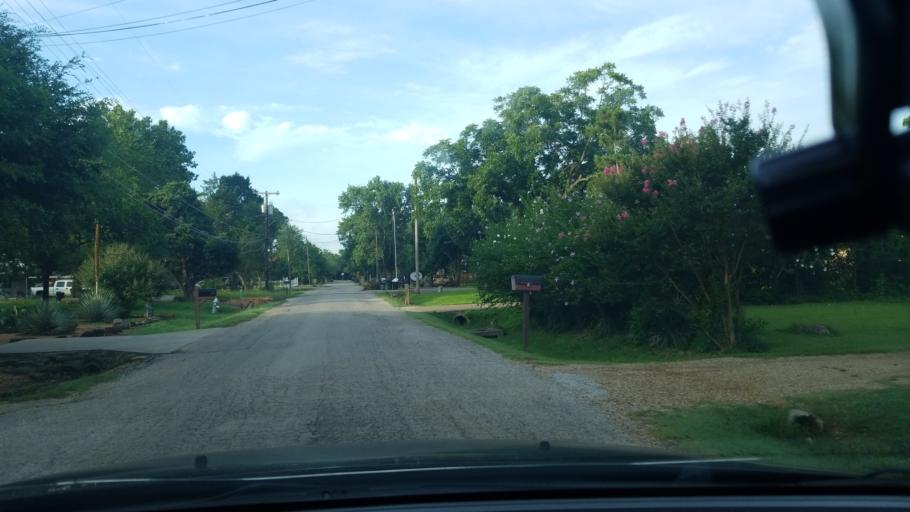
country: US
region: Texas
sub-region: Dallas County
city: Balch Springs
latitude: 32.7603
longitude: -96.6388
